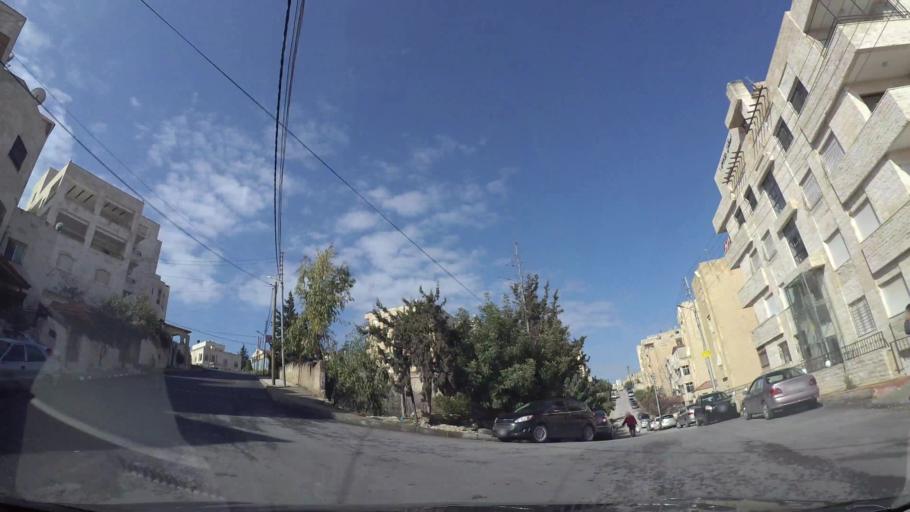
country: JO
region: Amman
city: Al Jubayhah
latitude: 32.0010
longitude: 35.8927
